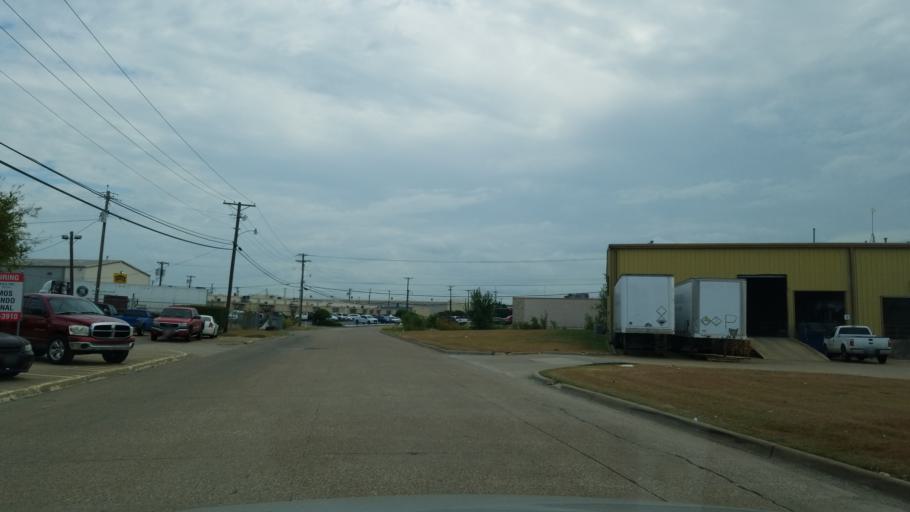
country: US
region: Texas
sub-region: Dallas County
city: Garland
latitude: 32.9045
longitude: -96.6860
